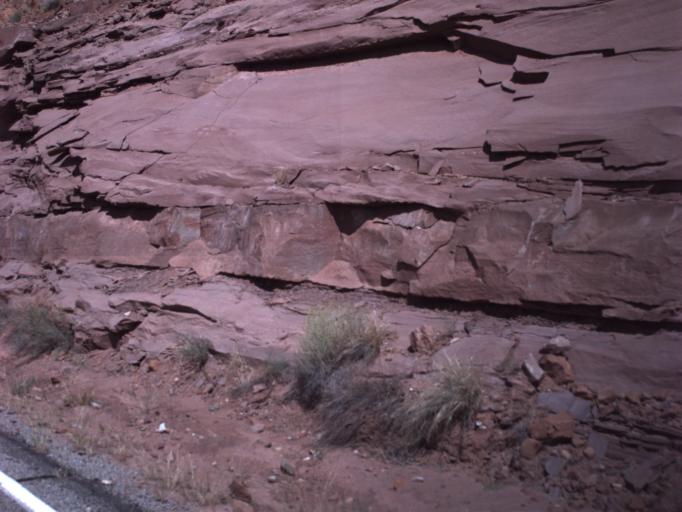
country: US
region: Utah
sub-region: Grand County
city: Moab
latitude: 38.5543
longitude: -109.6311
